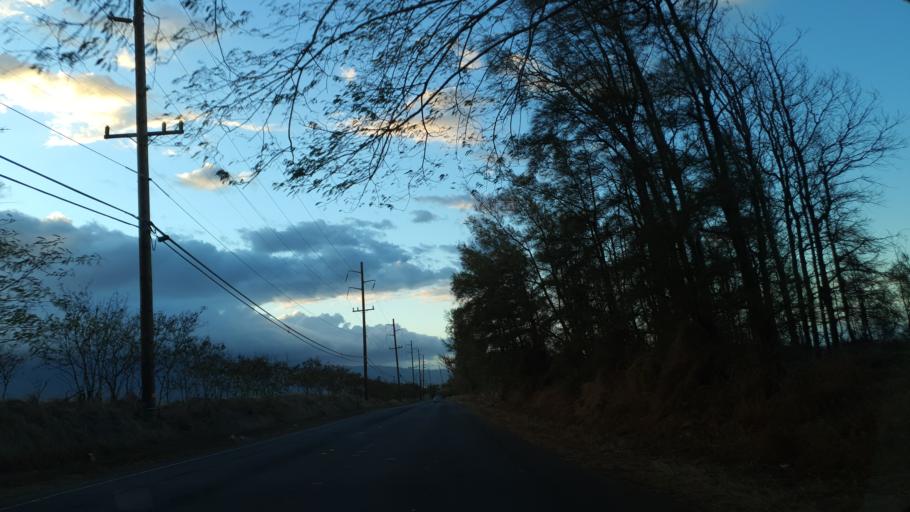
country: US
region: Hawaii
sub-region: Maui County
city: Kahului
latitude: 20.8682
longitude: -156.4350
